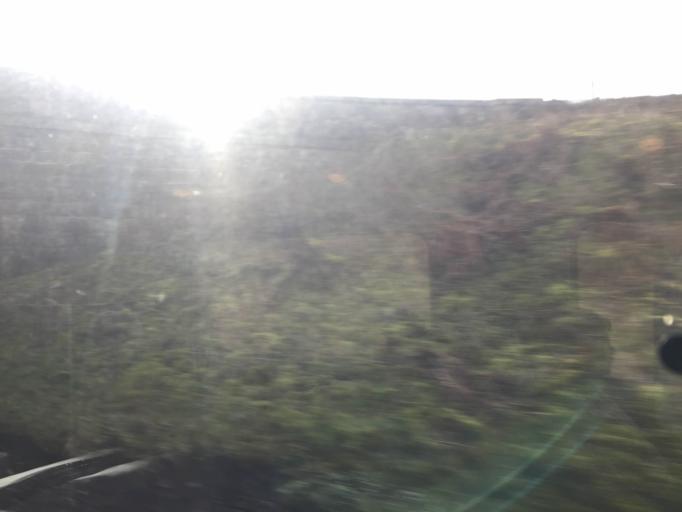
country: GB
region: England
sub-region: Cumbria
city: Kendal
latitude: 54.3550
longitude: -2.6850
